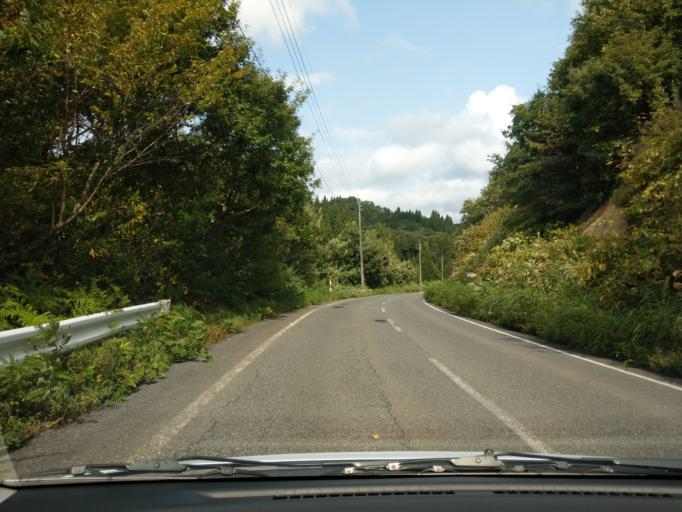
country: JP
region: Akita
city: Omagari
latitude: 39.4628
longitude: 140.3169
